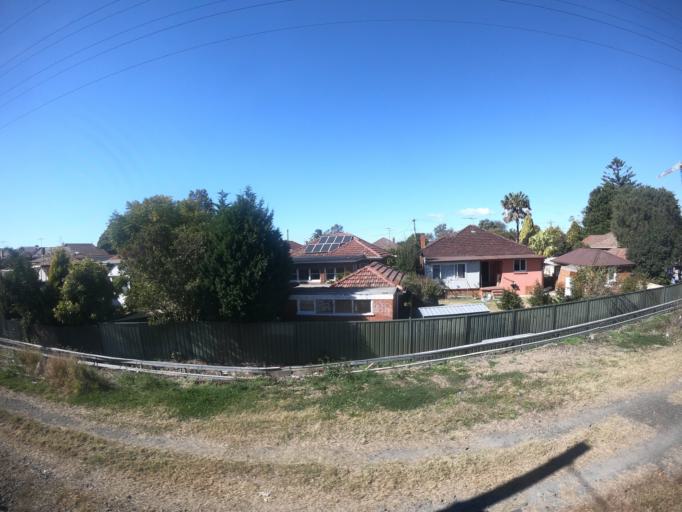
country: AU
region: New South Wales
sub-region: Hurstville
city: Penshurst
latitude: -33.9692
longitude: 151.0825
